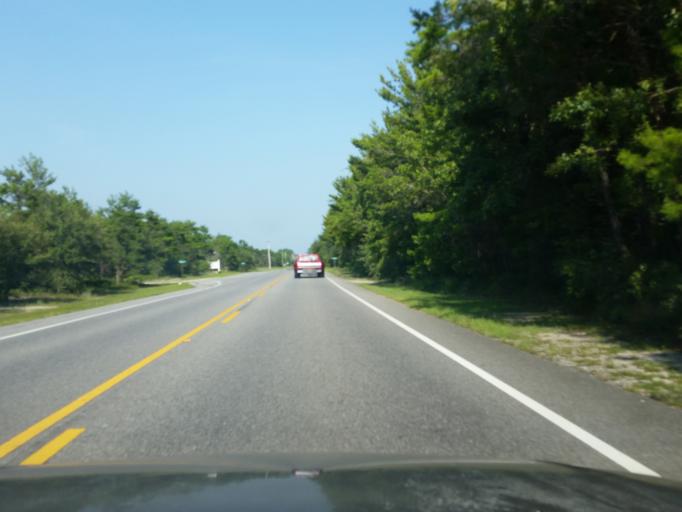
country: US
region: Alabama
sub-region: Baldwin County
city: Gulf Shores
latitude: 30.2537
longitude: -87.7406
